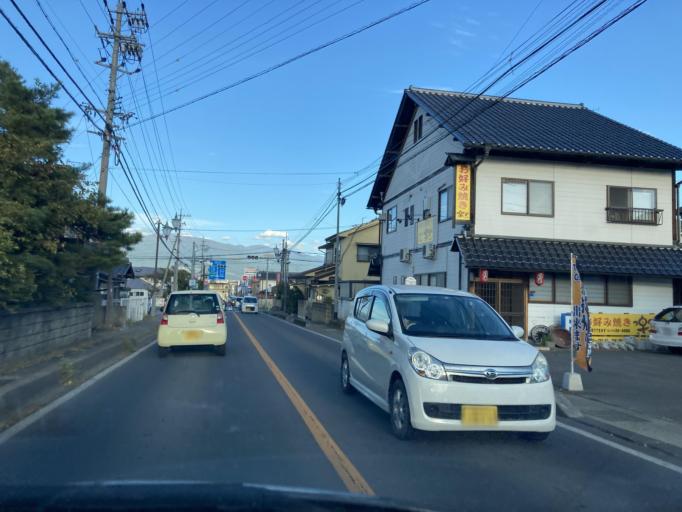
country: JP
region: Nagano
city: Ueda
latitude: 36.3884
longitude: 138.2044
